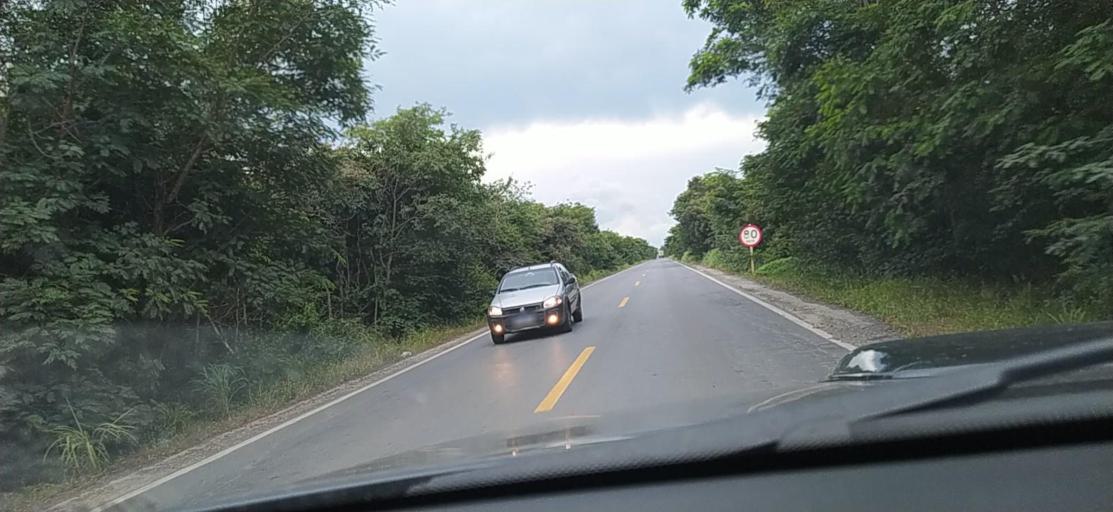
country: BR
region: Minas Gerais
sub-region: Francisco Sa
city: Francisco Sa
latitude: -16.2373
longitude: -43.6197
